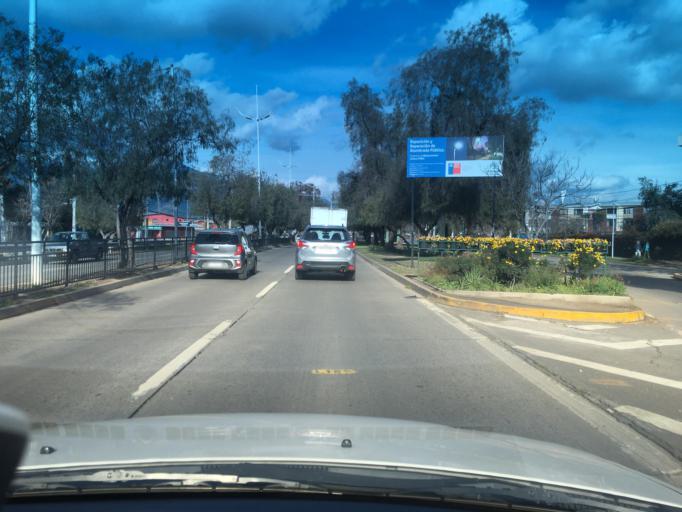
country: CL
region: Santiago Metropolitan
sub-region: Provincia de Santiago
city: Villa Presidente Frei, Nunoa, Santiago, Chile
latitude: -33.5185
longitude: -70.5829
